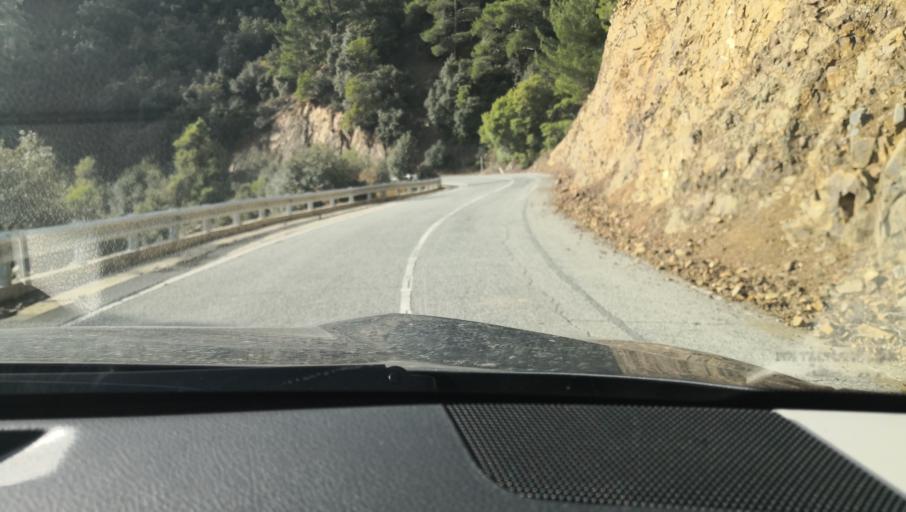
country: CY
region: Lefkosia
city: Lefka
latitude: 35.0129
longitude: 32.7306
